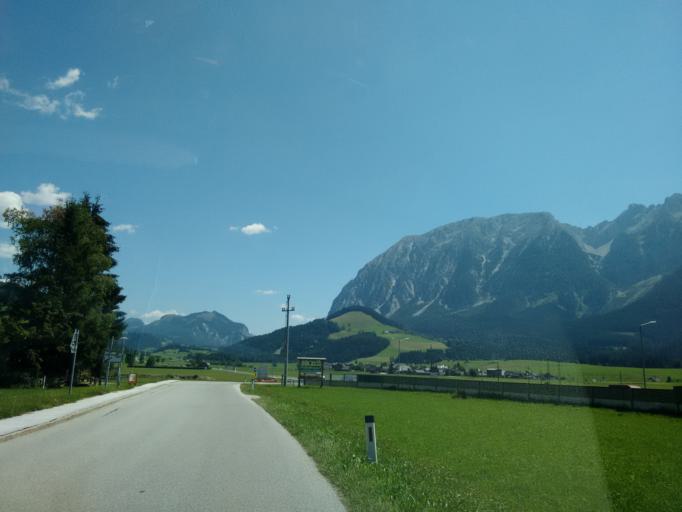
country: AT
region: Styria
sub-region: Politischer Bezirk Liezen
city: Tauplitz
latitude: 47.5527
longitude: 13.9618
